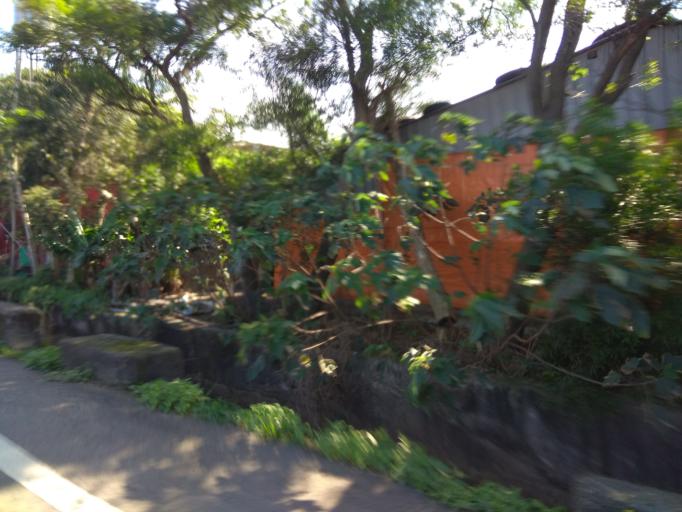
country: TW
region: Taiwan
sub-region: Hsinchu
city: Zhubei
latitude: 24.9503
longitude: 121.0152
